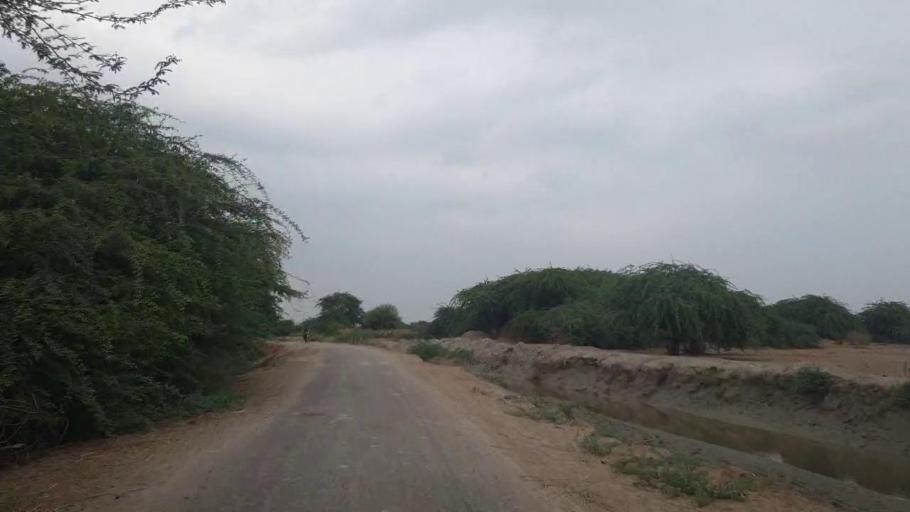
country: PK
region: Sindh
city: Badin
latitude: 24.6223
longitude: 68.6823
